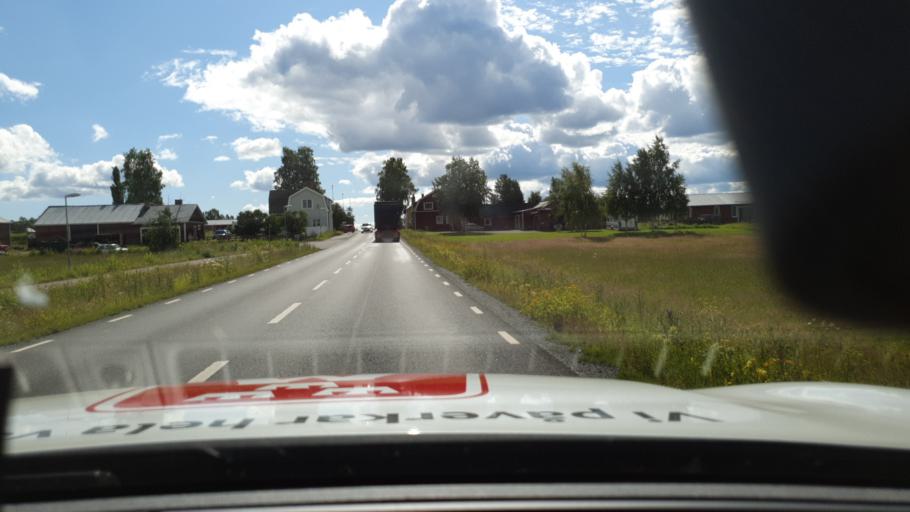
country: SE
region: Norrbotten
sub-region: Lulea Kommun
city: Sodra Sunderbyn
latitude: 65.8125
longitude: 22.0125
